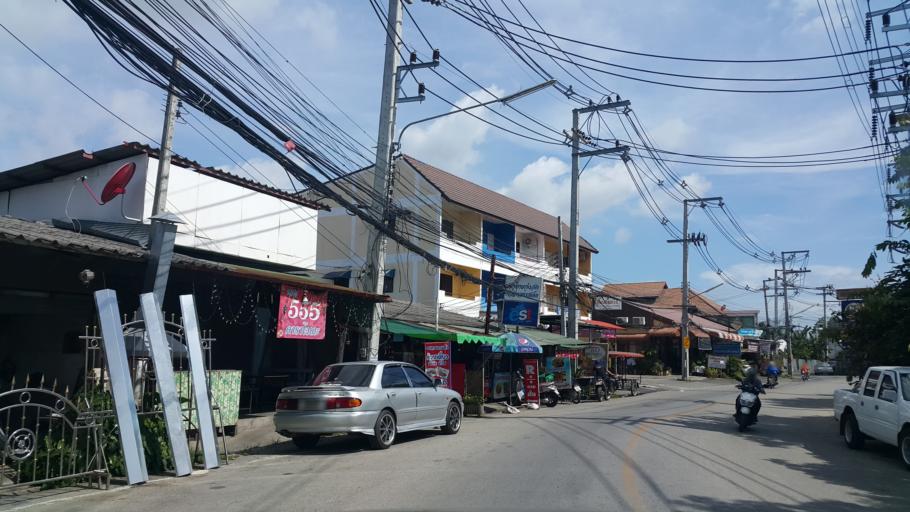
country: TH
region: Chiang Mai
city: Chiang Mai
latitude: 18.8028
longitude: 99.0118
